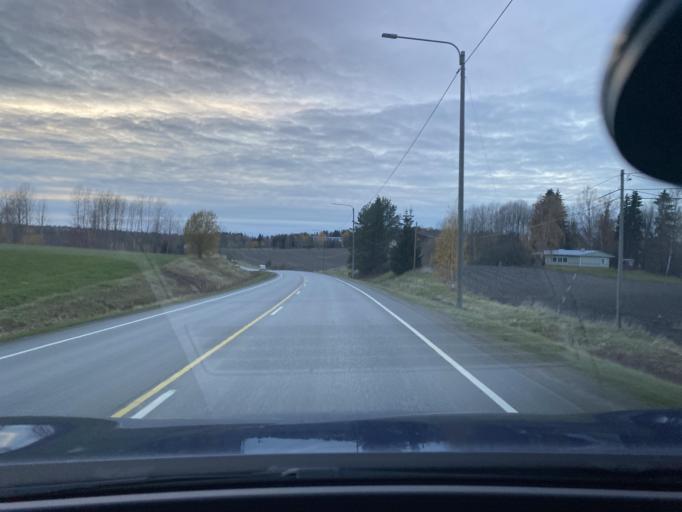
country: FI
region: Uusimaa
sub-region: Helsinki
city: Lohja
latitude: 60.3706
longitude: 24.1471
